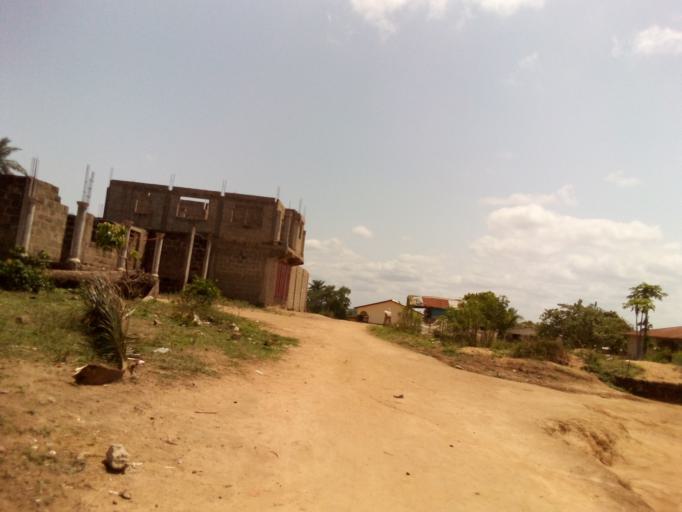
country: SL
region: Western Area
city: Waterloo
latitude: 8.3404
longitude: -13.0297
